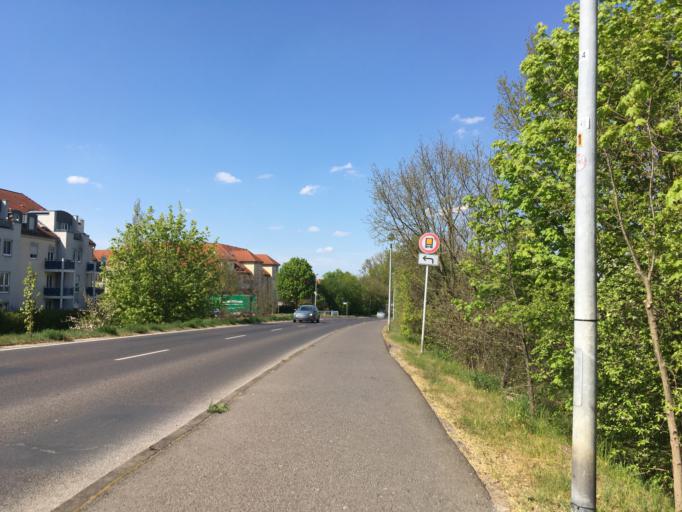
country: DE
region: Brandenburg
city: Werneuchen
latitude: 52.6194
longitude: 13.6749
